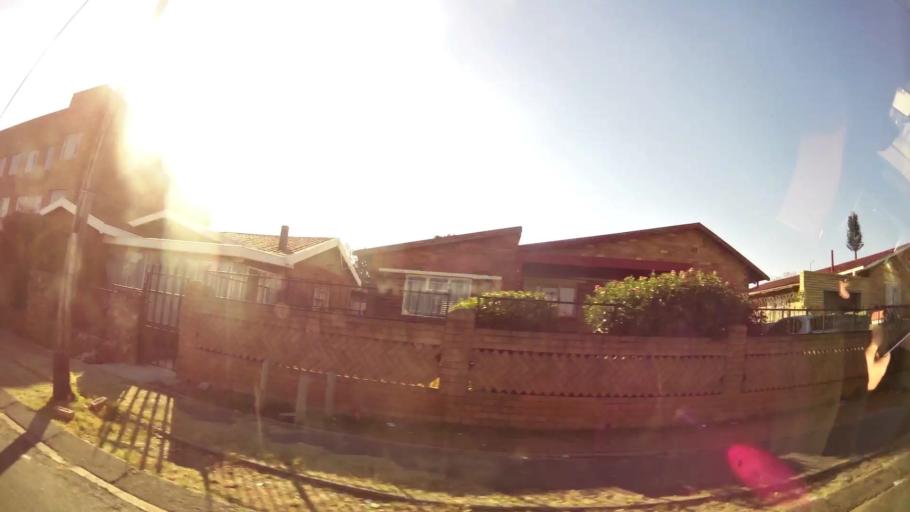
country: ZA
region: Gauteng
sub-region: City of Johannesburg Metropolitan Municipality
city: Johannesburg
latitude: -26.2127
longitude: 27.9808
